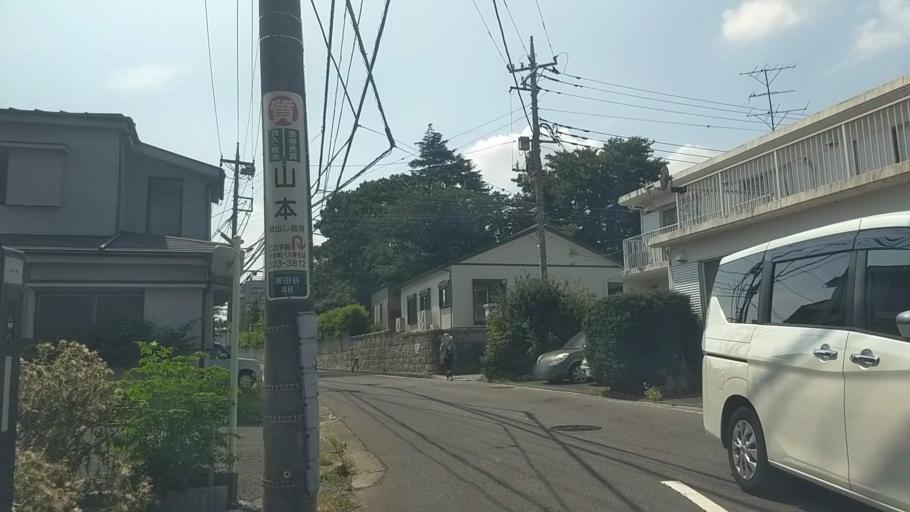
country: JP
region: Kanagawa
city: Yokohama
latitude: 35.4815
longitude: 139.6164
